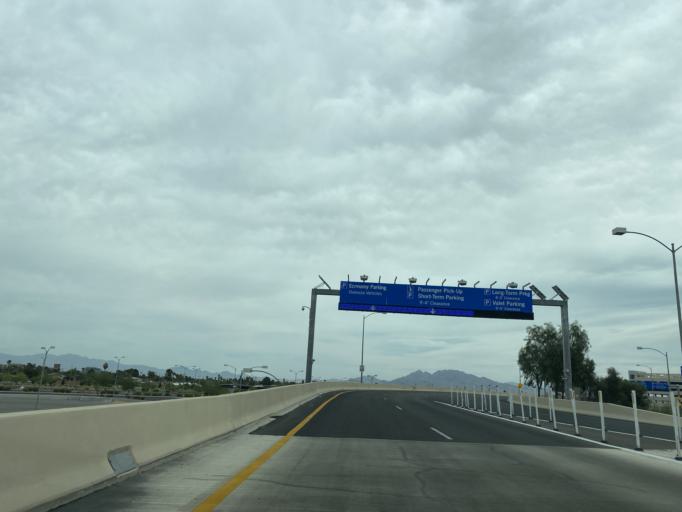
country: US
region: Nevada
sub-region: Clark County
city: Paradise
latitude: 36.0874
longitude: -115.1433
